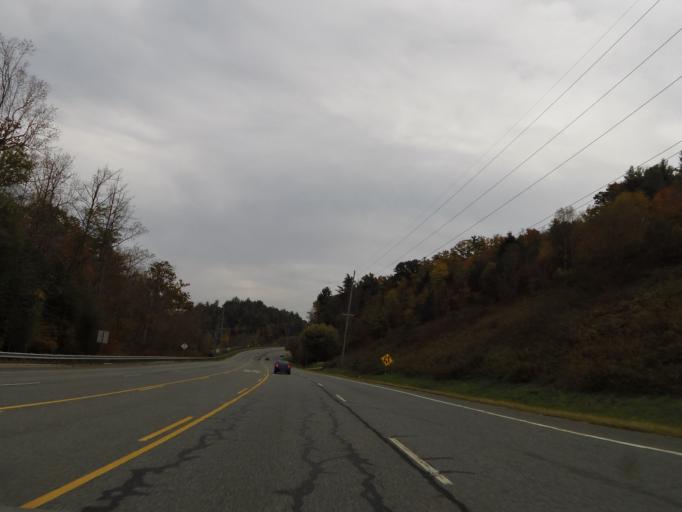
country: US
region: North Carolina
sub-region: Caldwell County
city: Lenoir
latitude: 36.0085
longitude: -81.5712
